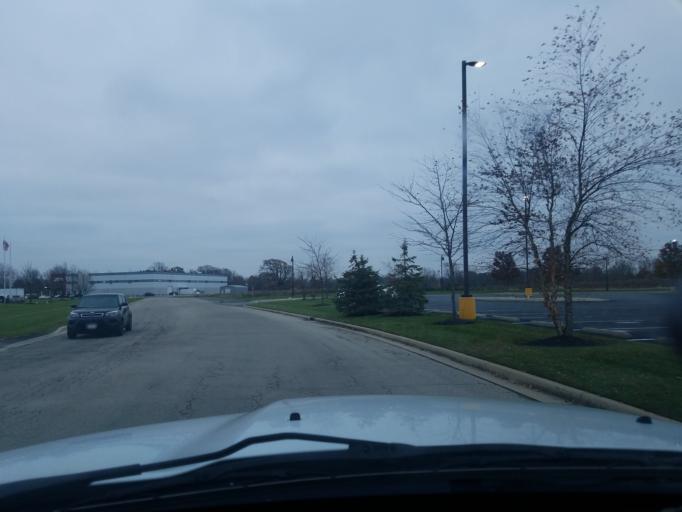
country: US
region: Indiana
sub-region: Delaware County
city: Muncie
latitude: 40.2287
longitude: -85.3946
